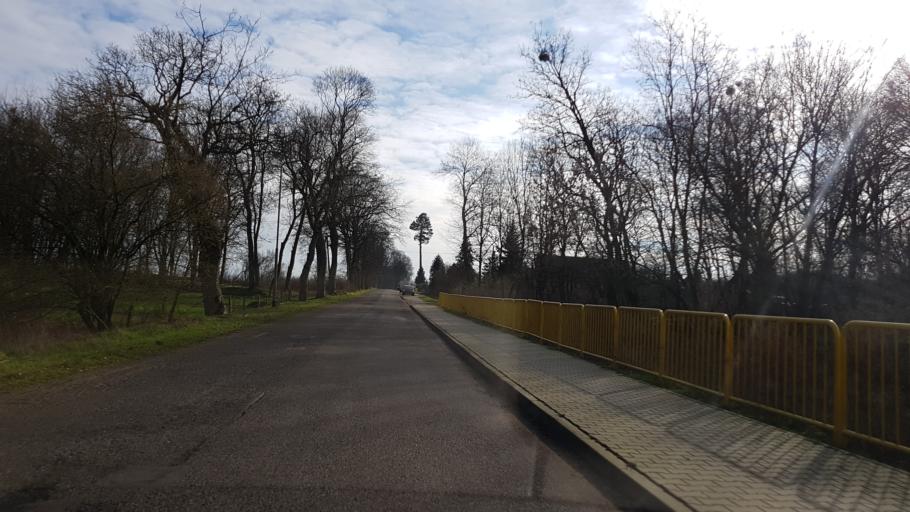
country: PL
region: West Pomeranian Voivodeship
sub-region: Powiat policki
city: Dobra
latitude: 53.5536
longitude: 14.3096
